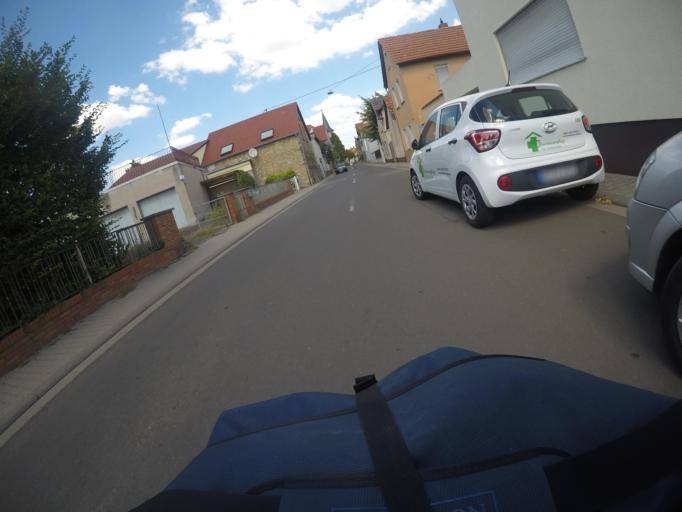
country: DE
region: Rheinland-Pfalz
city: Guntersblum
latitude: 49.7942
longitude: 8.3454
